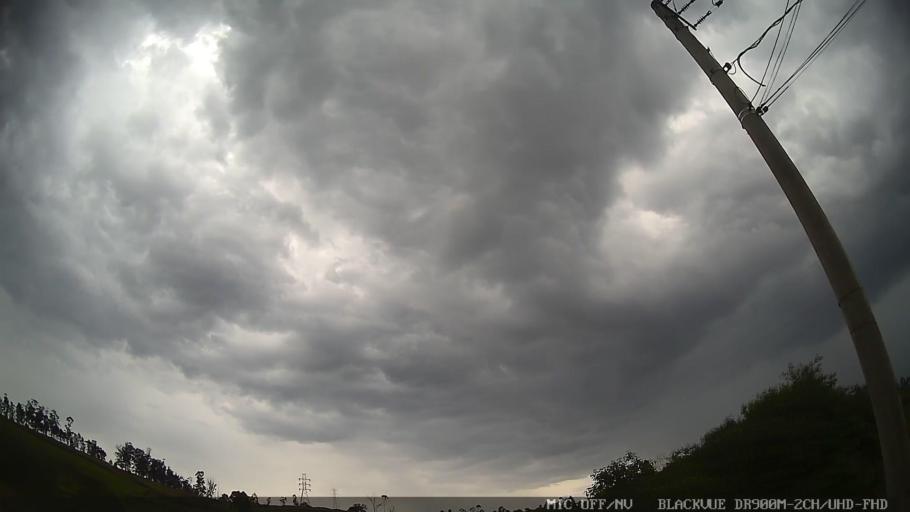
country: BR
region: Sao Paulo
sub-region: Itatiba
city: Itatiba
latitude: -23.0059
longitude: -46.8598
